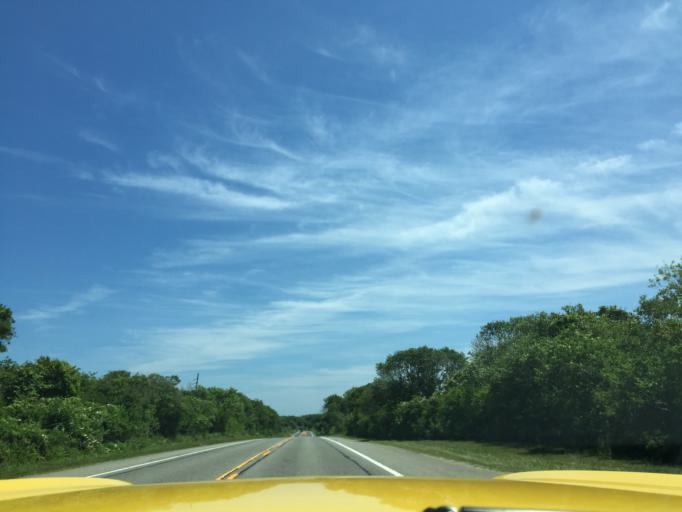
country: US
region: New York
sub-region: Suffolk County
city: Montauk
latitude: 41.0456
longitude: -71.9183
